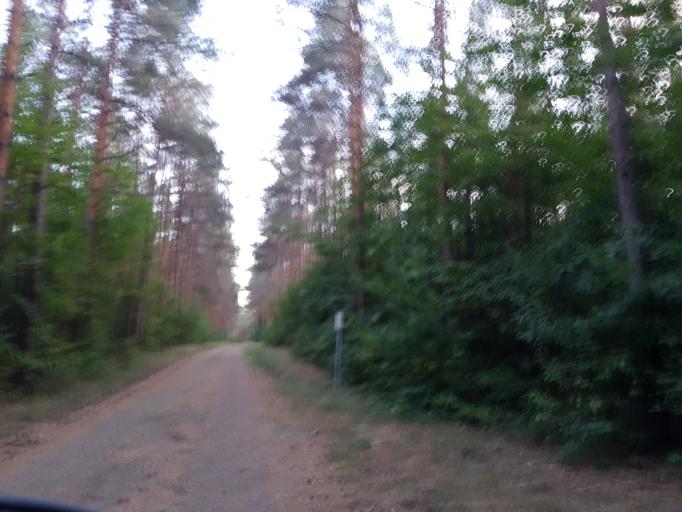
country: DE
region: Brandenburg
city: Trobitz
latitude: 51.5729
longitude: 13.4456
